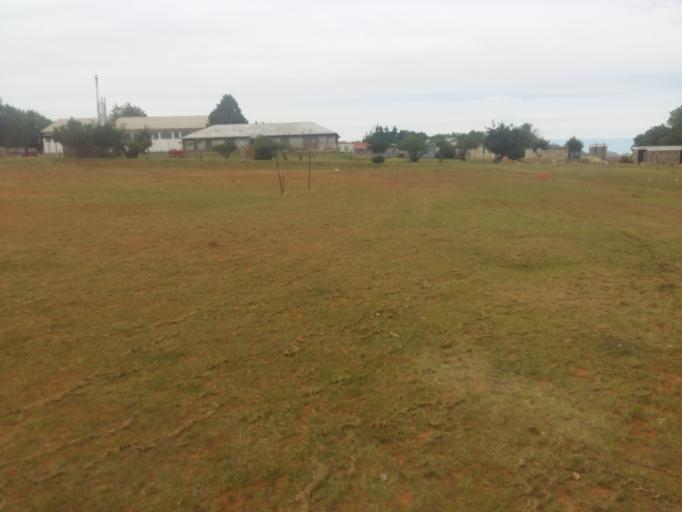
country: LS
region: Mafeteng
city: Mafeteng
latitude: -29.6978
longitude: 27.4311
